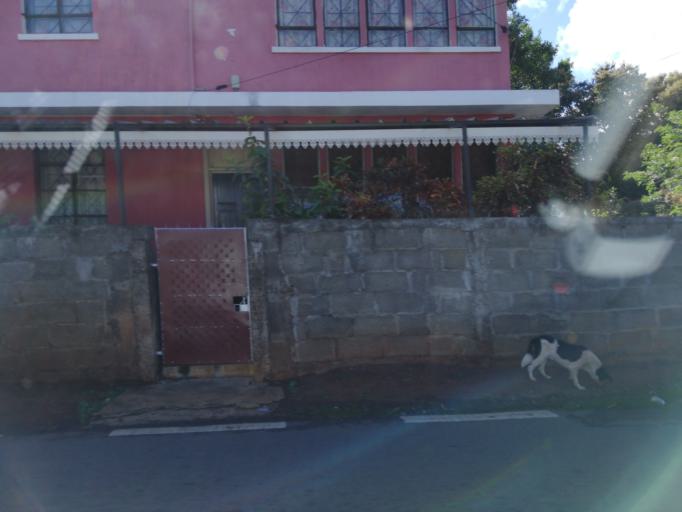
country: MU
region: Moka
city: Pailles
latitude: -20.1826
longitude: 57.4754
